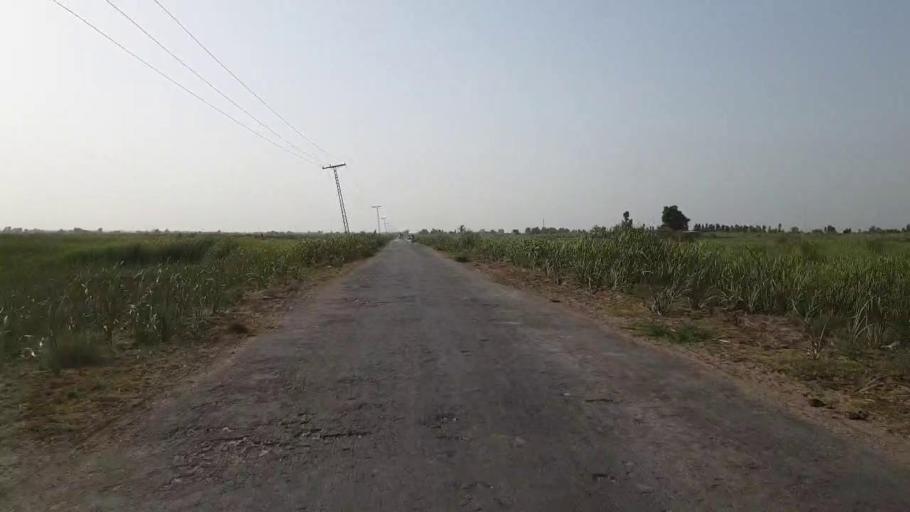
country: PK
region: Sindh
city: Jam Sahib
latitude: 26.4112
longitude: 68.8748
